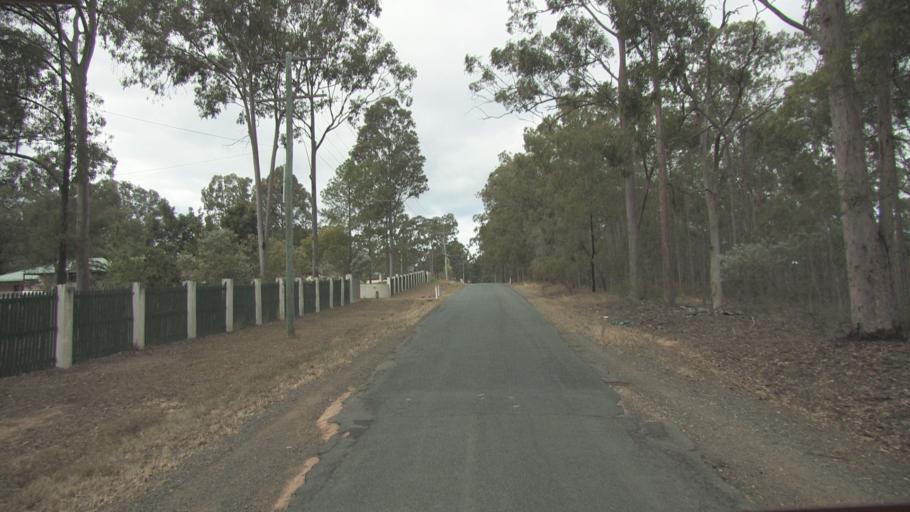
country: AU
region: Queensland
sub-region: Logan
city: Cedar Vale
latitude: -27.8799
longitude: 153.0321
